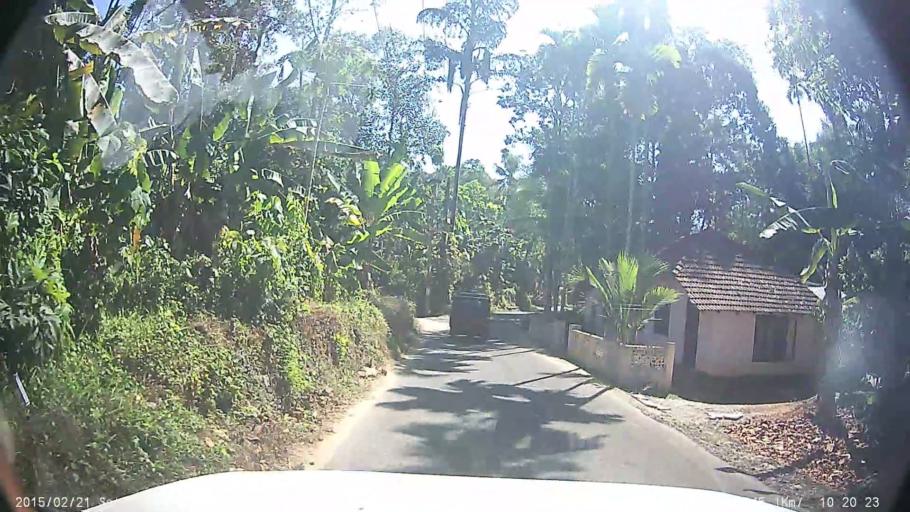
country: IN
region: Kerala
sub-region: Kottayam
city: Palackattumala
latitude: 9.8699
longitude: 76.6626
